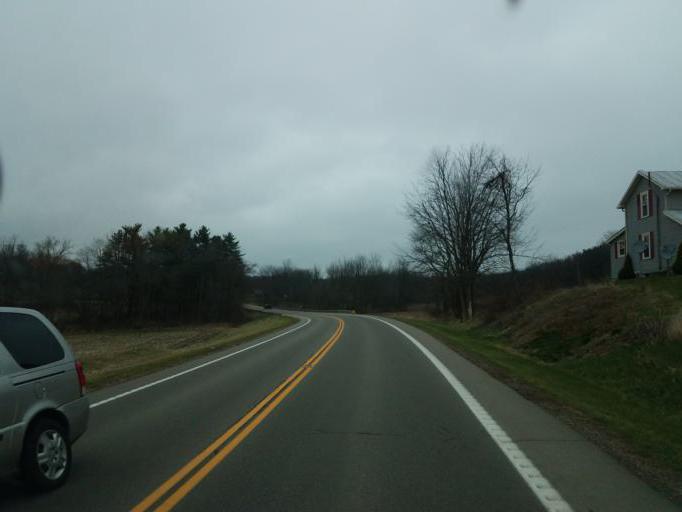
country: US
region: Ohio
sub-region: Ashland County
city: Loudonville
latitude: 40.7089
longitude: -82.2413
